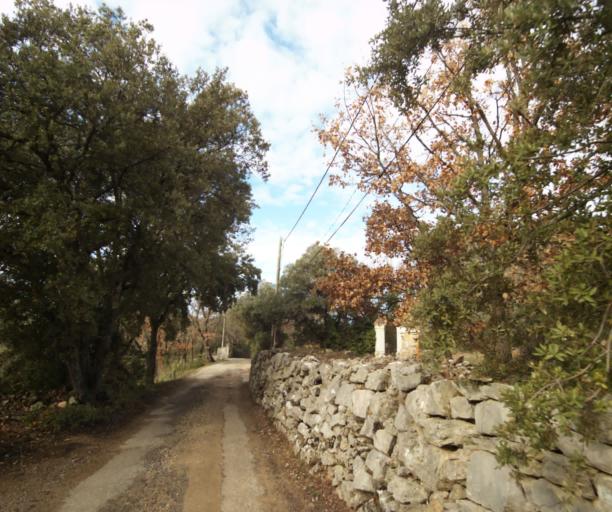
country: FR
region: Provence-Alpes-Cote d'Azur
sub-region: Departement du Var
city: Trans-en-Provence
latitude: 43.5058
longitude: 6.4756
